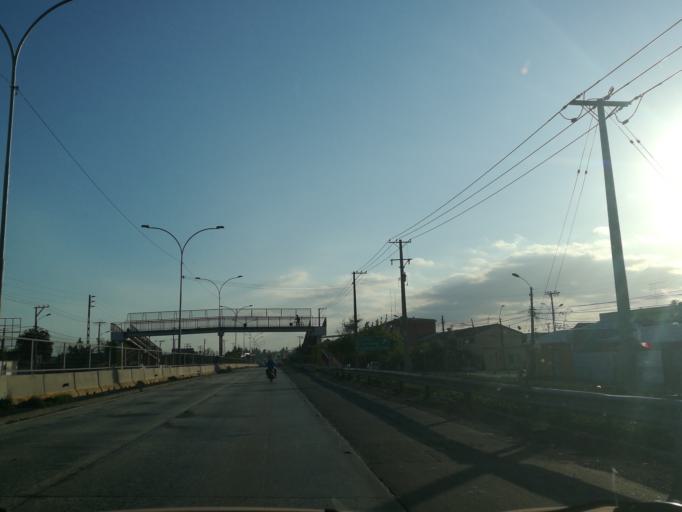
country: CL
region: O'Higgins
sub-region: Provincia de Cachapoal
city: Rancagua
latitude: -34.1813
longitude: -70.7363
